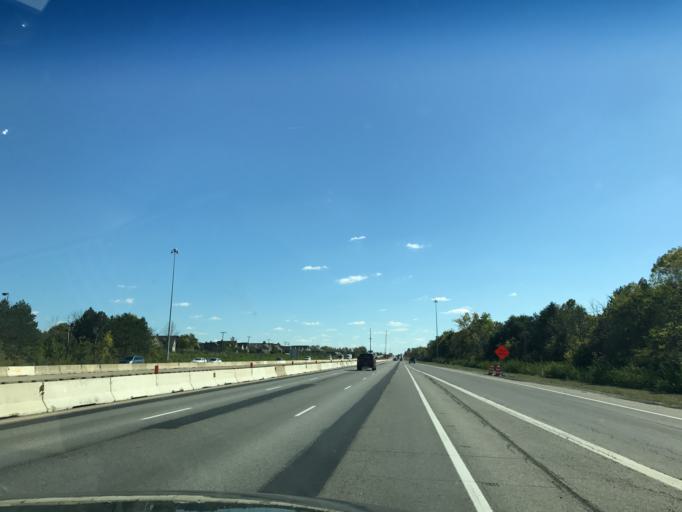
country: US
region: Ohio
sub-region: Franklin County
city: Dublin
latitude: 40.0726
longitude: -83.1349
